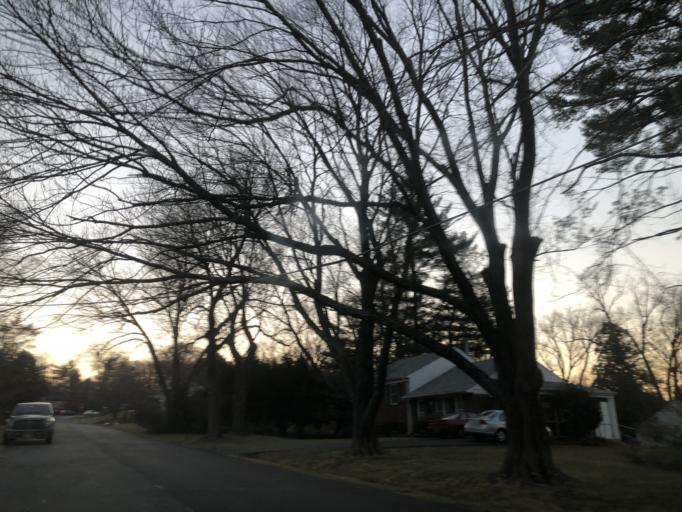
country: US
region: Virginia
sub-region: Fairfax County
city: Pimmit Hills
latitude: 38.9025
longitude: -77.1972
